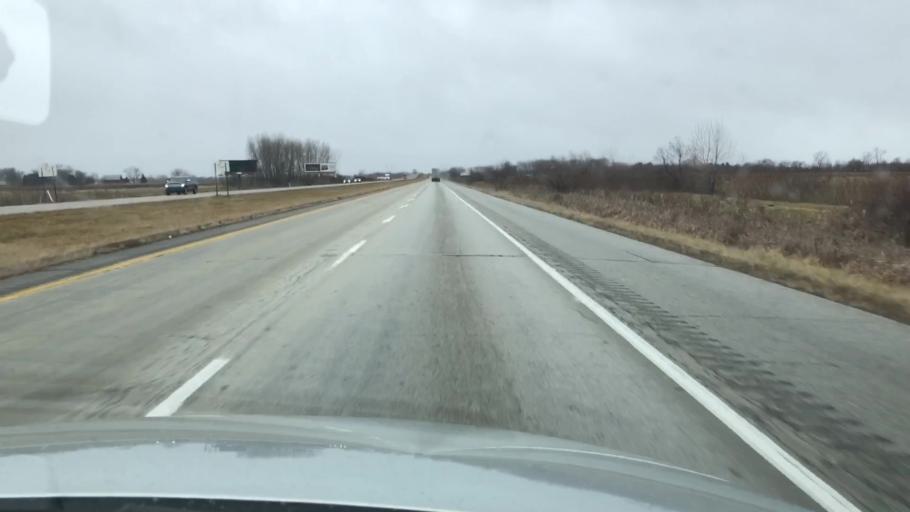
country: US
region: Indiana
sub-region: Starke County
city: Knox
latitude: 41.3941
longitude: -86.6070
